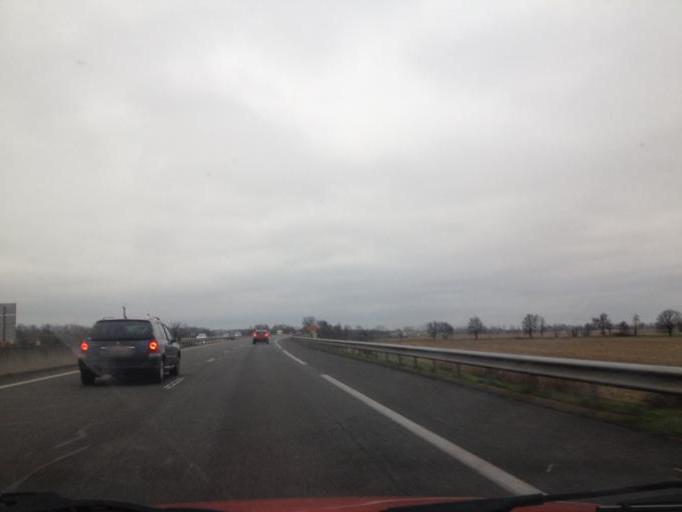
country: FR
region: Auvergne
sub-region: Departement de l'Allier
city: Toulon-sur-Allier
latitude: 46.5165
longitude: 3.3543
